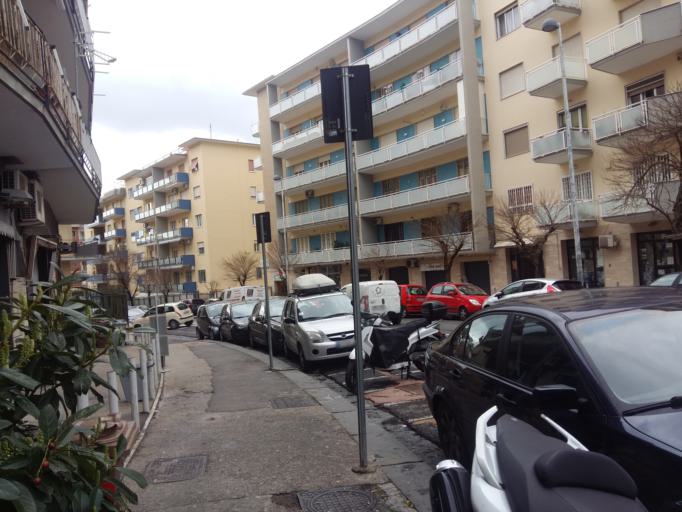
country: IT
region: Campania
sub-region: Provincia di Napoli
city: Napoli
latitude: 40.8581
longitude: 14.2278
